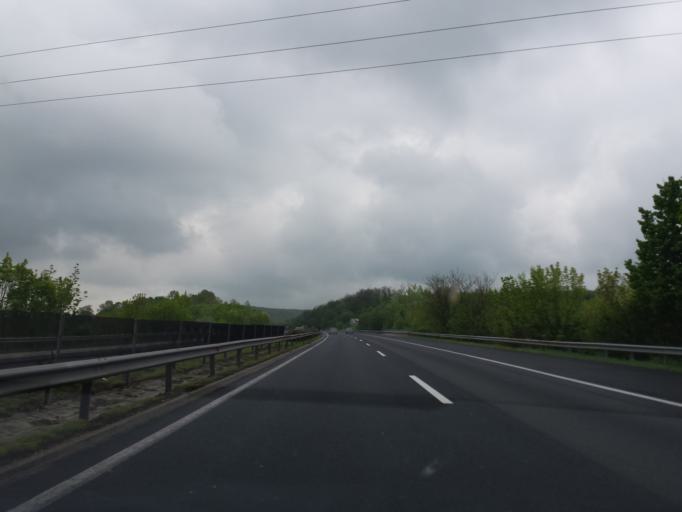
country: HU
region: Fejer
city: Szarliget
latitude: 47.5334
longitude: 18.5010
